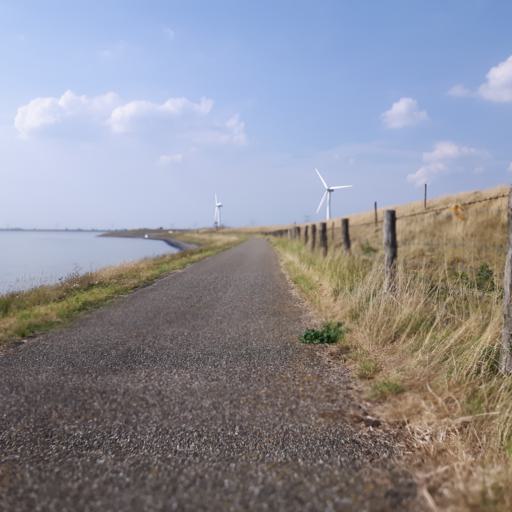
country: NL
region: Zeeland
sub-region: Gemeente Reimerswaal
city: Yerseke
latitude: 51.4517
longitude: 3.9929
